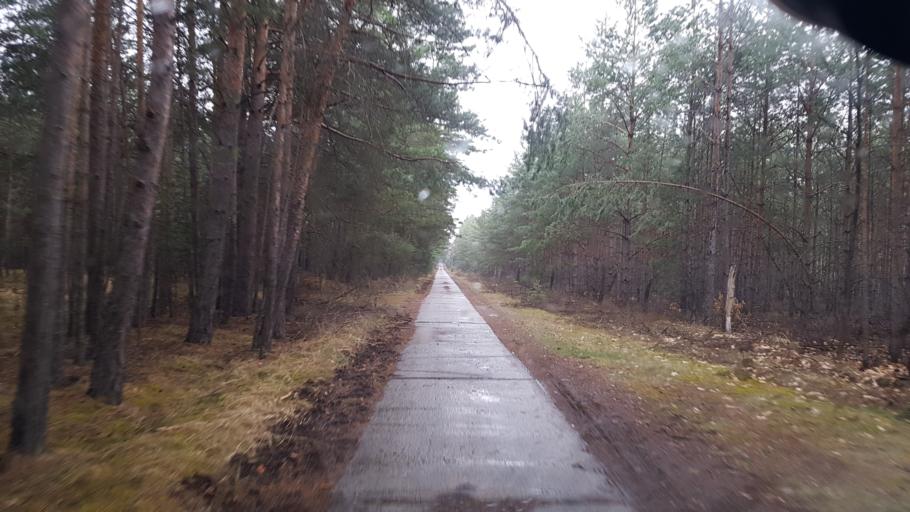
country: DE
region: Brandenburg
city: Grossraschen
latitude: 51.6035
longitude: 13.9901
